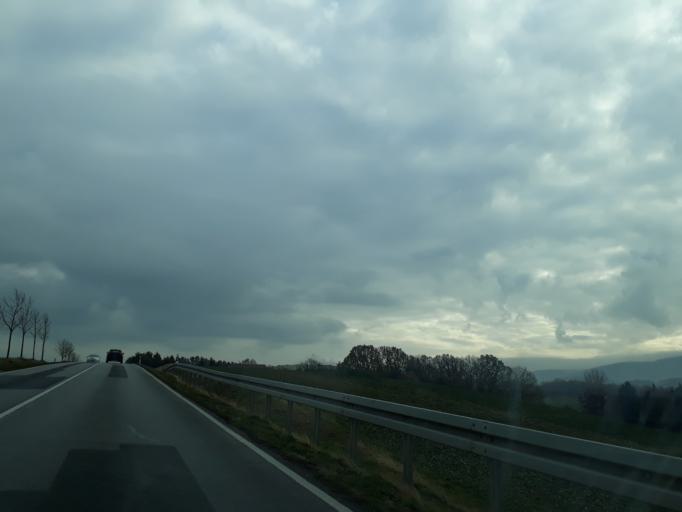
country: DE
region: Saxony
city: Kubschutz
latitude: 51.1678
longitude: 14.4916
